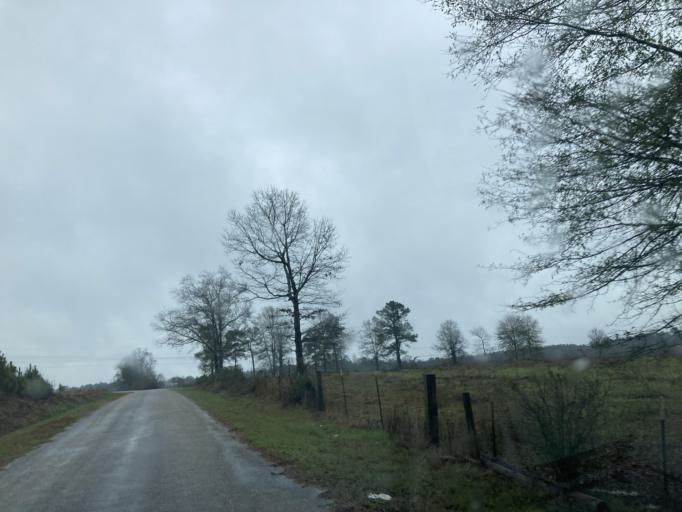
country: US
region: Mississippi
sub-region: Forrest County
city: Rawls Springs
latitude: 31.4803
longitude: -89.3907
